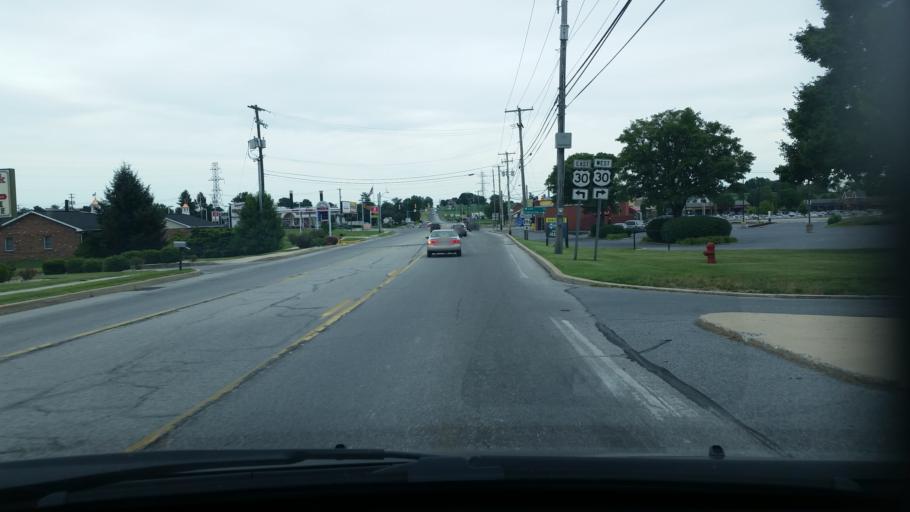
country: US
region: Pennsylvania
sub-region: Lancaster County
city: Strasburg
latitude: 40.0241
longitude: -76.1936
